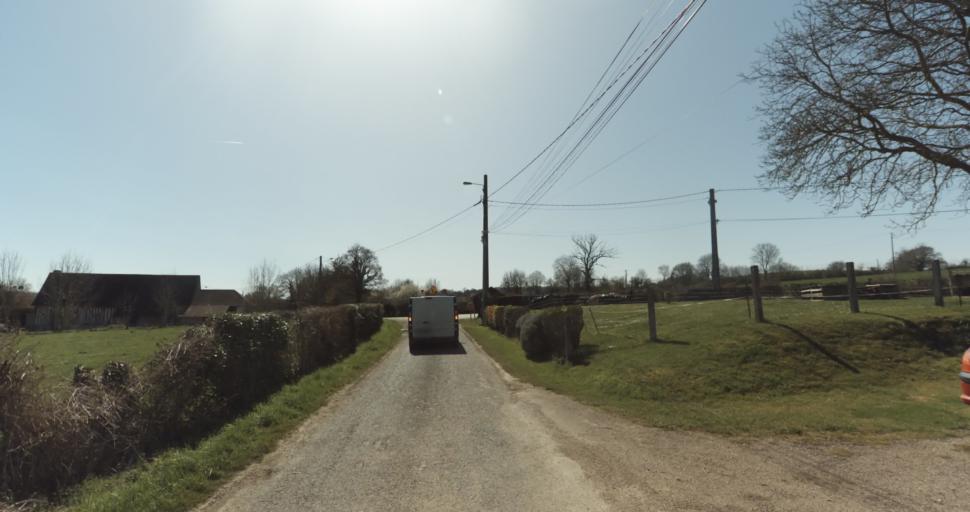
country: FR
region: Lower Normandy
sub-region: Departement du Calvados
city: Saint-Pierre-sur-Dives
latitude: 48.9898
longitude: 0.0276
